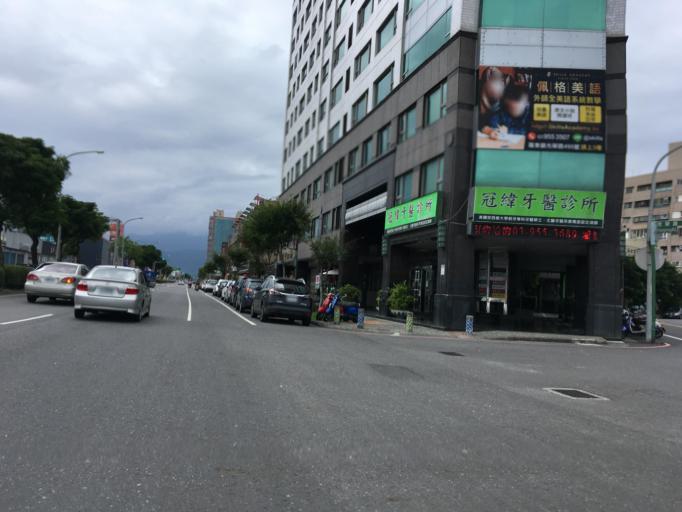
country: TW
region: Taiwan
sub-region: Yilan
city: Yilan
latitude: 24.6815
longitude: 121.7777
